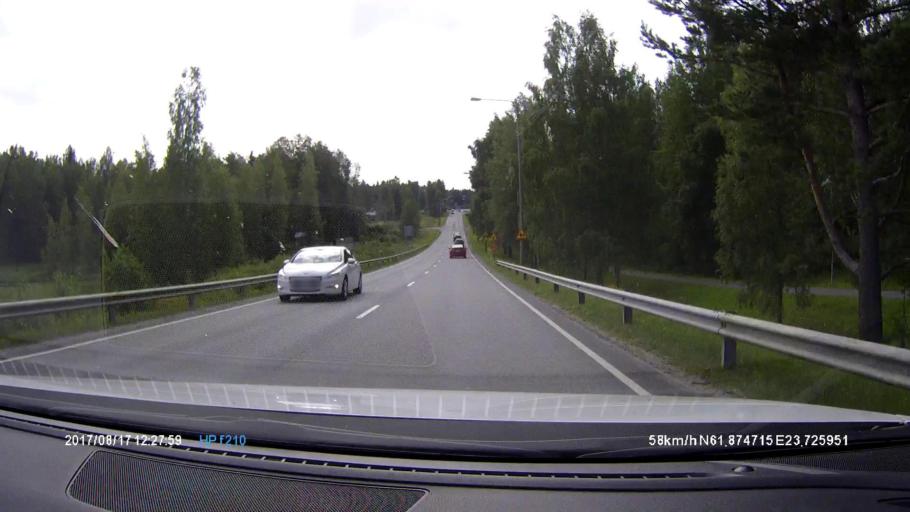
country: FI
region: Pirkanmaa
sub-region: Tampere
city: Kuru
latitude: 61.8744
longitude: 23.7260
